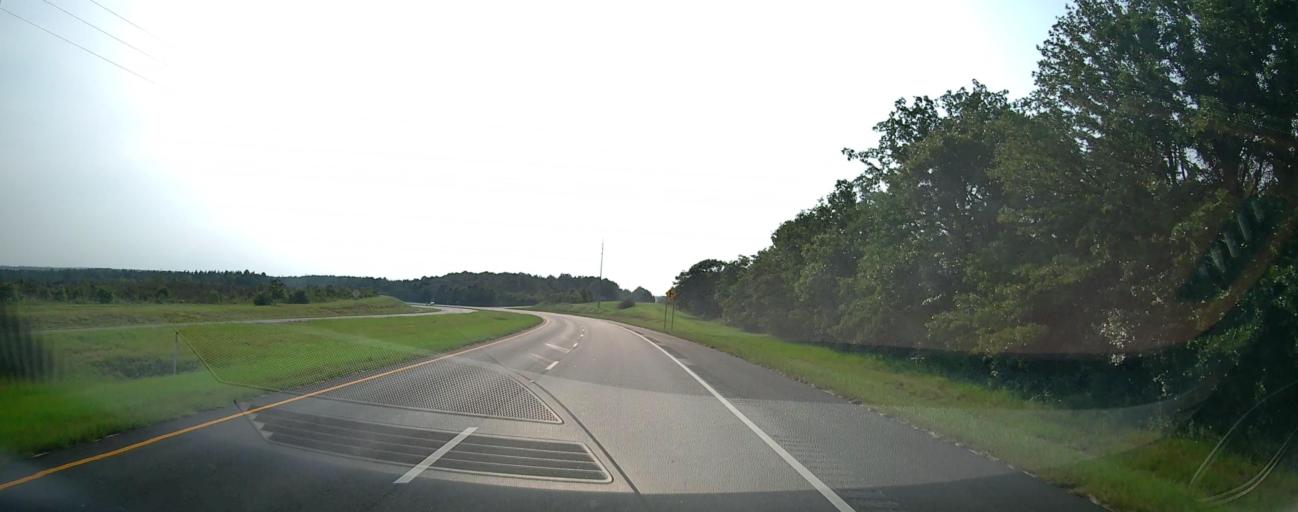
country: US
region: Georgia
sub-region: Taylor County
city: Butler
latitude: 32.5886
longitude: -84.3532
